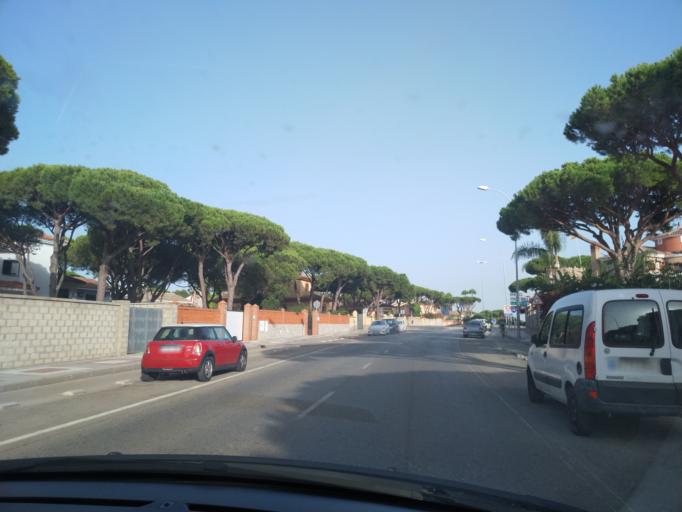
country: ES
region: Andalusia
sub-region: Provincia de Cadiz
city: Chiclana de la Frontera
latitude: 36.3775
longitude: -6.1880
